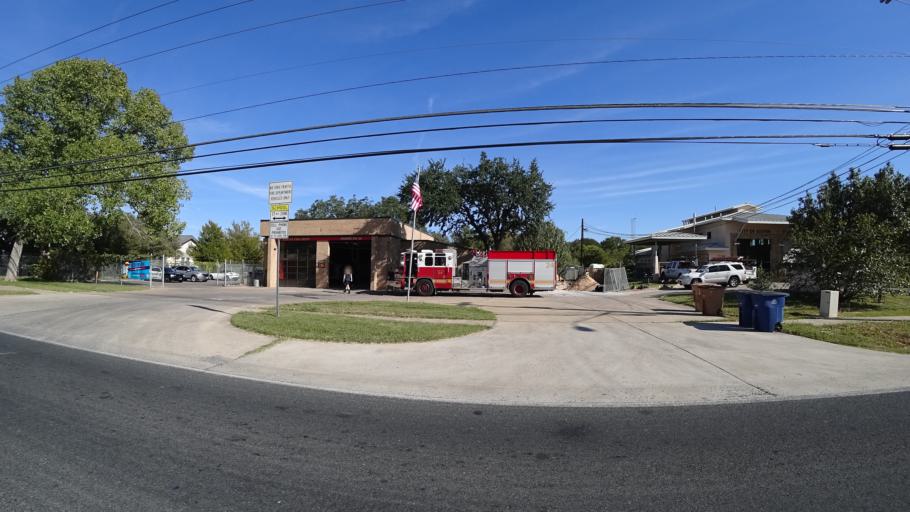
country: US
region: Texas
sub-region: Travis County
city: Onion Creek
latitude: 30.1873
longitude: -97.7427
